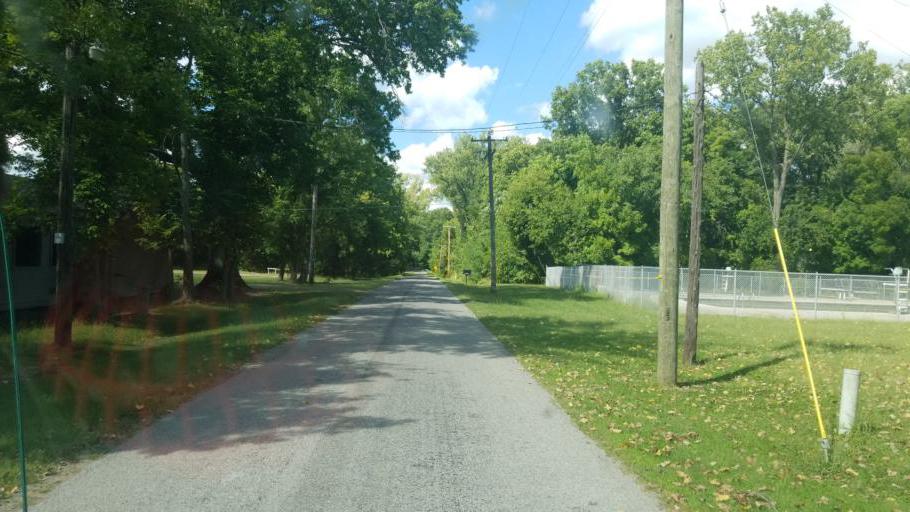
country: US
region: Ohio
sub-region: Union County
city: Richwood
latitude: 40.3437
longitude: -83.2533
